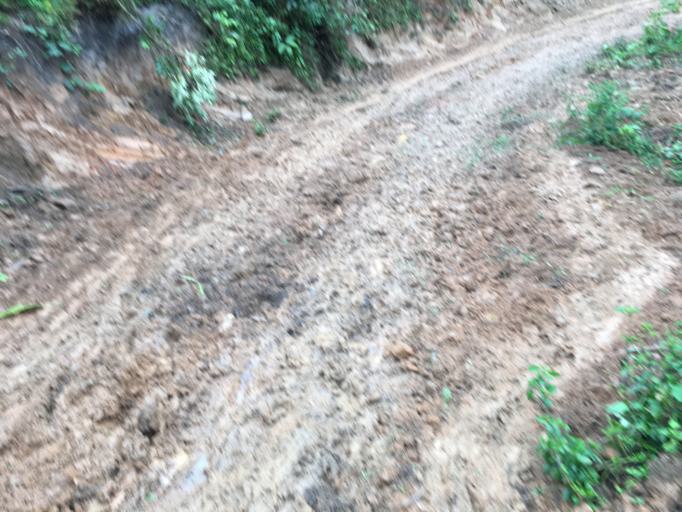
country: LA
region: Houaphan
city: Xamtay
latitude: 19.8988
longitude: 104.4600
